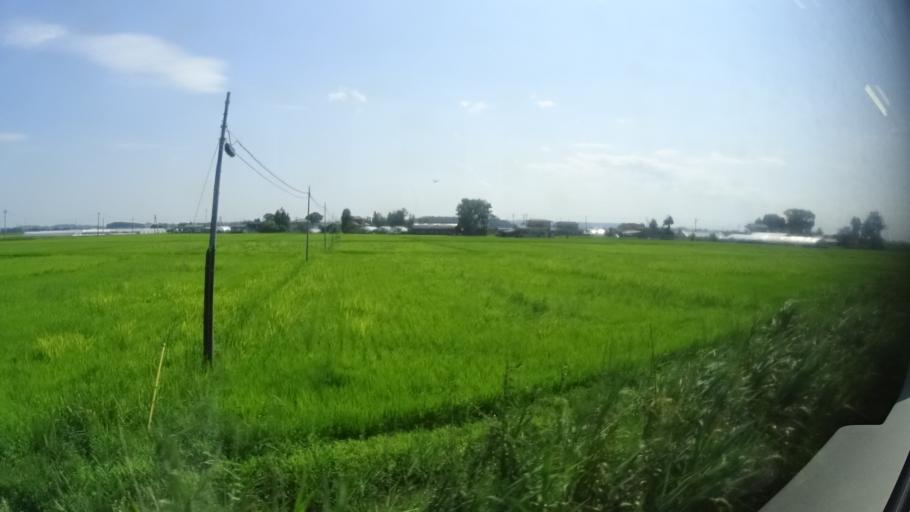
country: JP
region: Miyagi
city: Kogota
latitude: 38.5504
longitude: 141.0848
